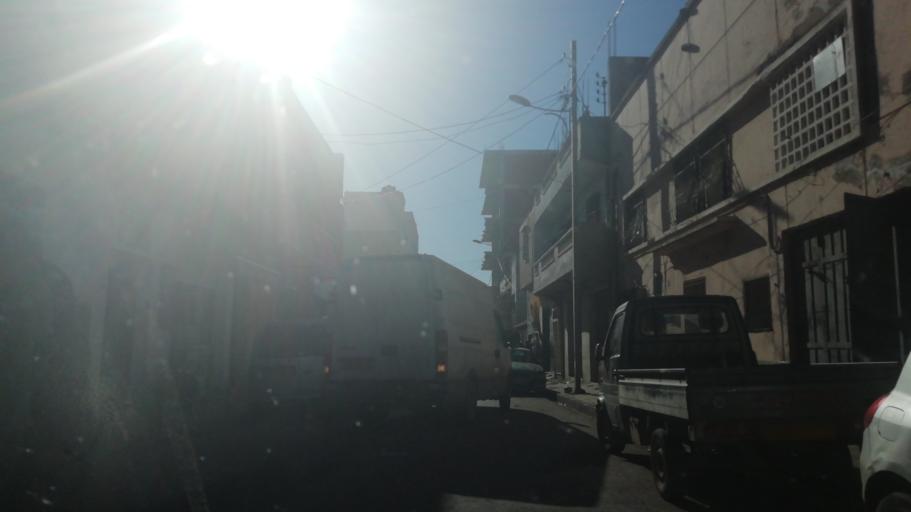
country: DZ
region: Oran
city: Oran
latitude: 35.6790
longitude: -0.6510
